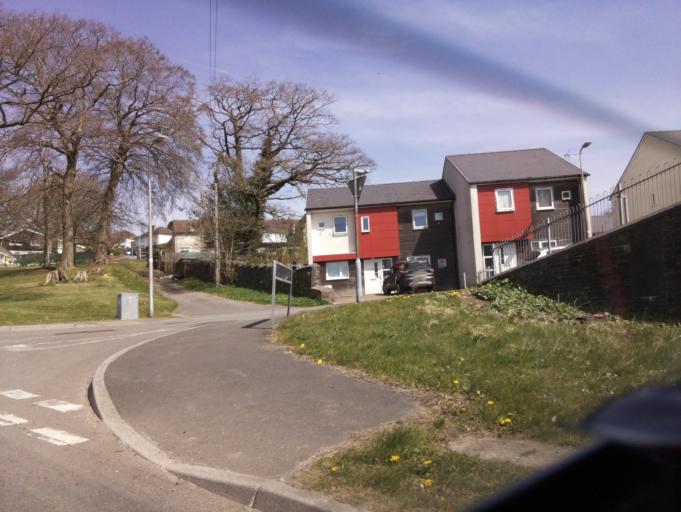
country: GB
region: Wales
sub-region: Merthyr Tydfil County Borough
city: Merthyr Tydfil
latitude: 51.7606
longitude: -3.3720
